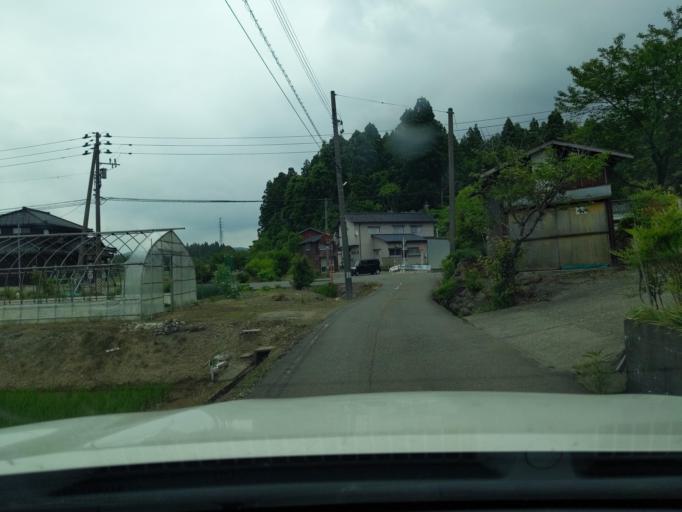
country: JP
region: Niigata
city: Kashiwazaki
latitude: 37.3419
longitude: 138.5892
